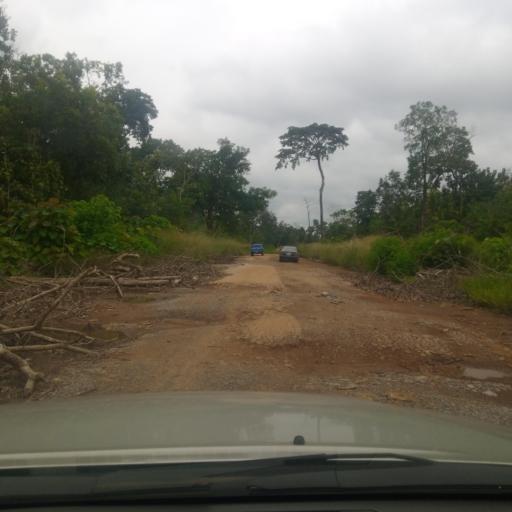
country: NG
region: Ebonyi
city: Effium
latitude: 6.6249
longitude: 8.0486
